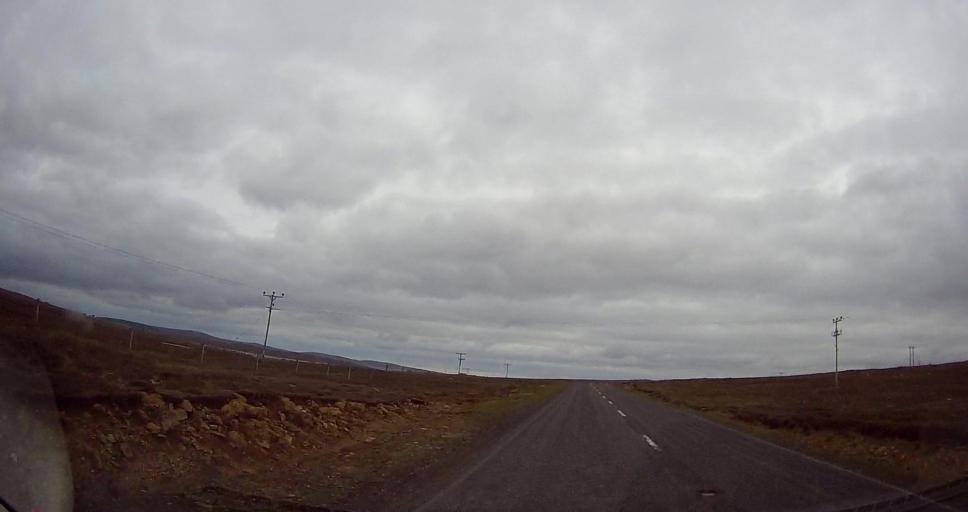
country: GB
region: Scotland
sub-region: Shetland Islands
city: Shetland
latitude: 60.7120
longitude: -0.9168
